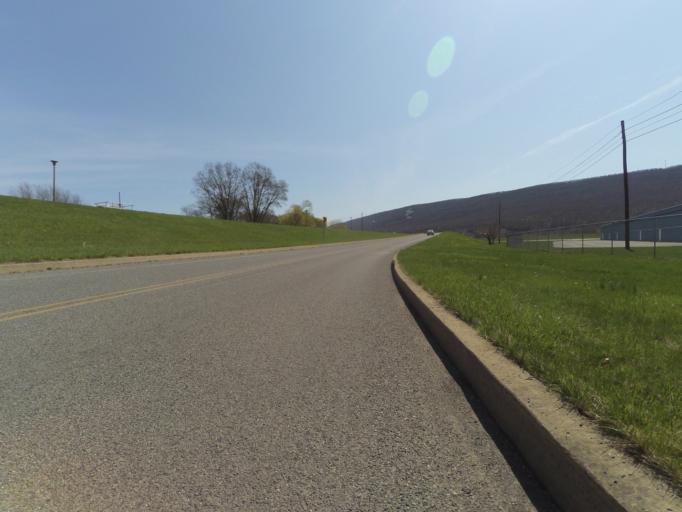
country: US
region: Pennsylvania
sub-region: Clinton County
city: Dunnstown
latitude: 41.1385
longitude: -77.4196
